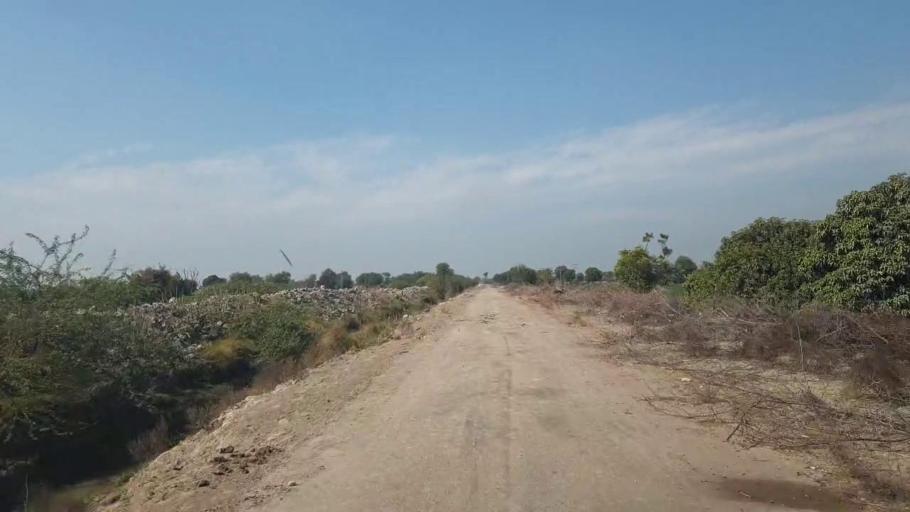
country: PK
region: Sindh
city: Shahdadpur
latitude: 25.9983
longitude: 68.5216
